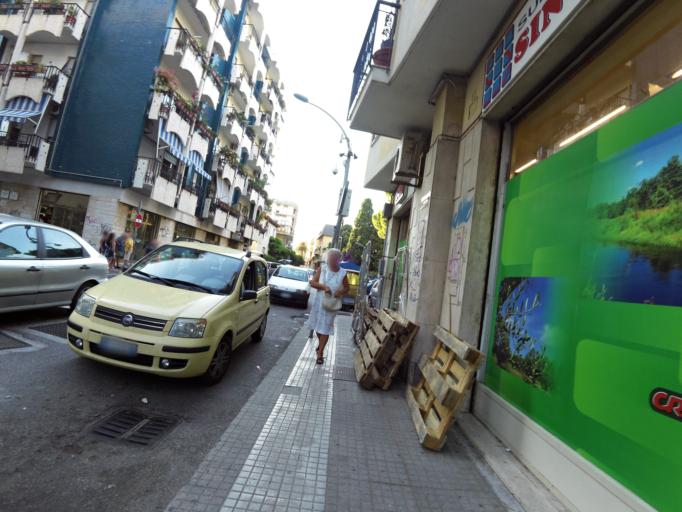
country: IT
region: Calabria
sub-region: Provincia di Catanzaro
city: Soverato Marina
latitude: 38.6881
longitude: 16.5514
